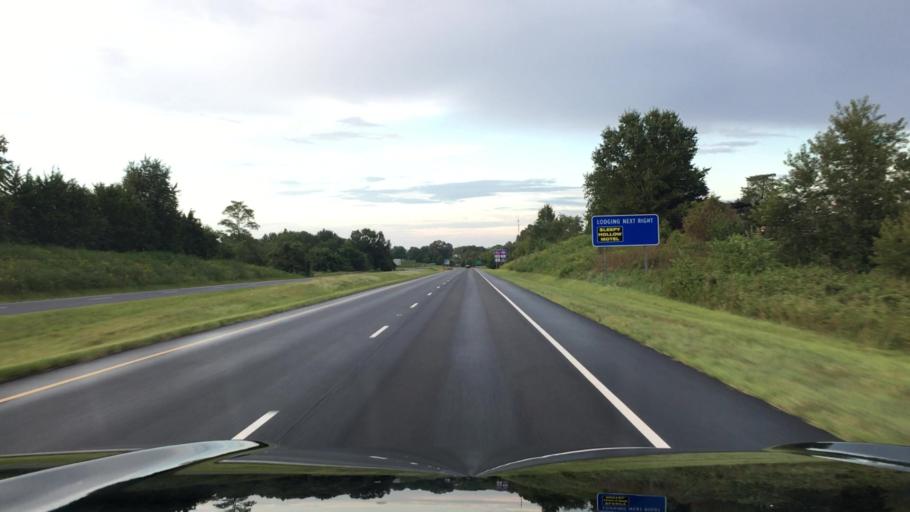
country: US
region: Virginia
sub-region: Culpeper County
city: Culpeper
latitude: 38.4812
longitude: -77.9434
